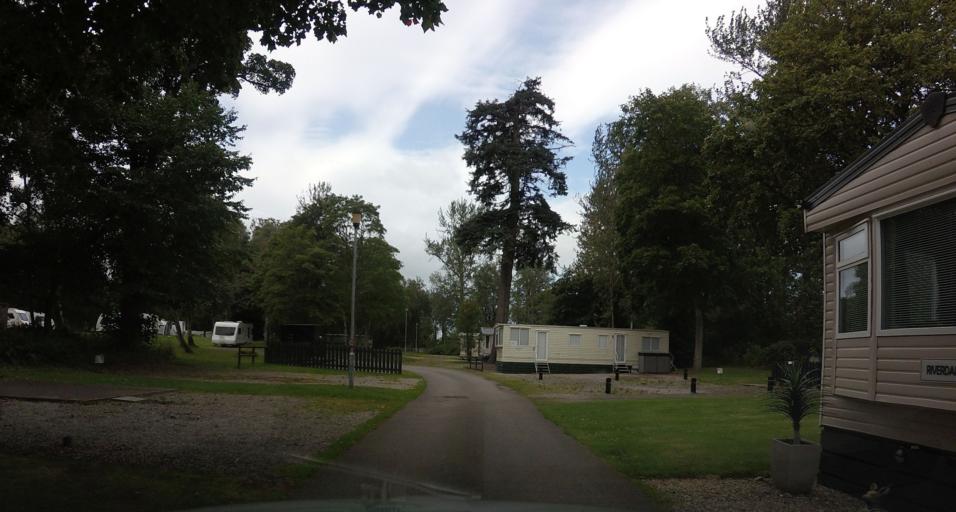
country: GB
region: Scotland
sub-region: Aberdeenshire
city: Alford
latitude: 57.2418
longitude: -2.6949
